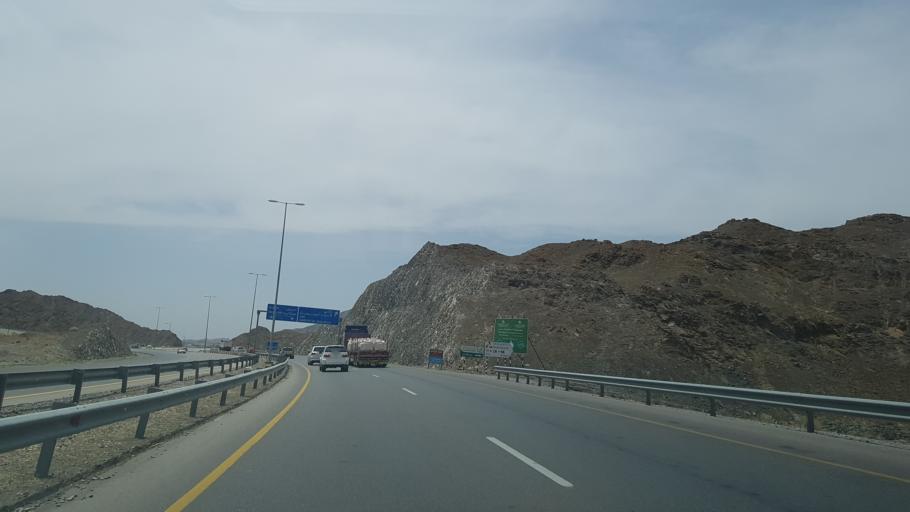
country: OM
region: Muhafazat ad Dakhiliyah
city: Izki
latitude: 22.9770
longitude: 57.7819
